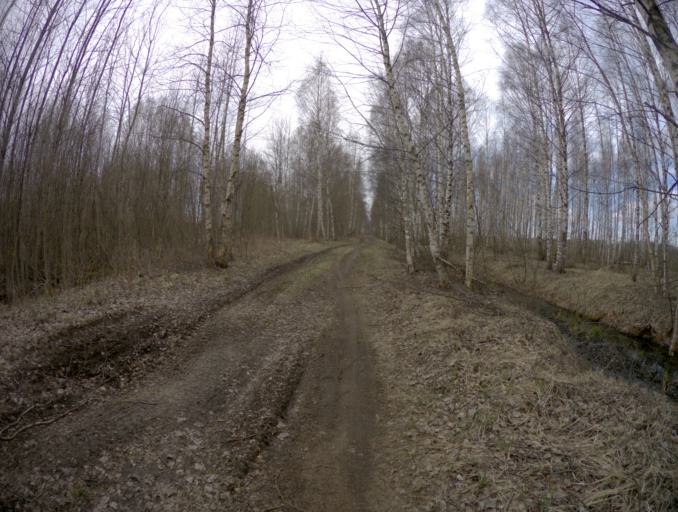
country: RU
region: Vladimir
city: Raduzhnyy
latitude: 55.9114
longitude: 40.2396
